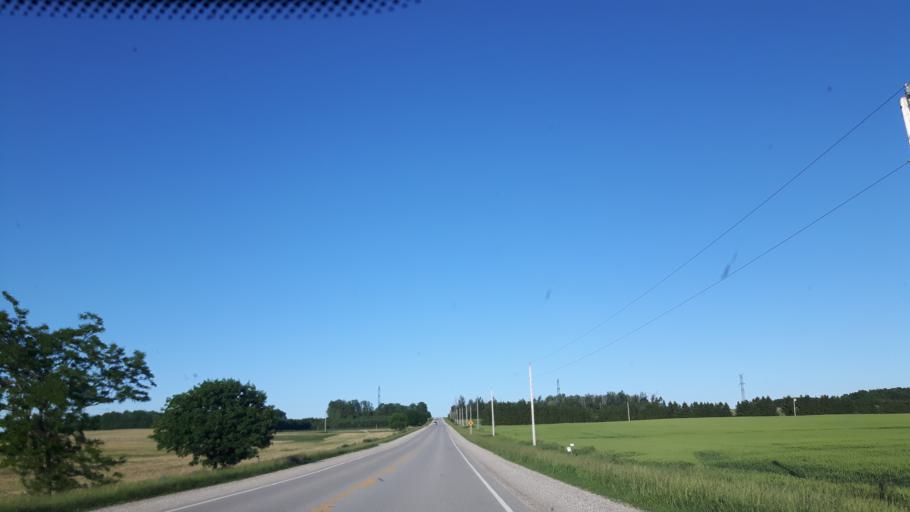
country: CA
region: Ontario
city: Goderich
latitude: 43.6427
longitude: -81.6479
